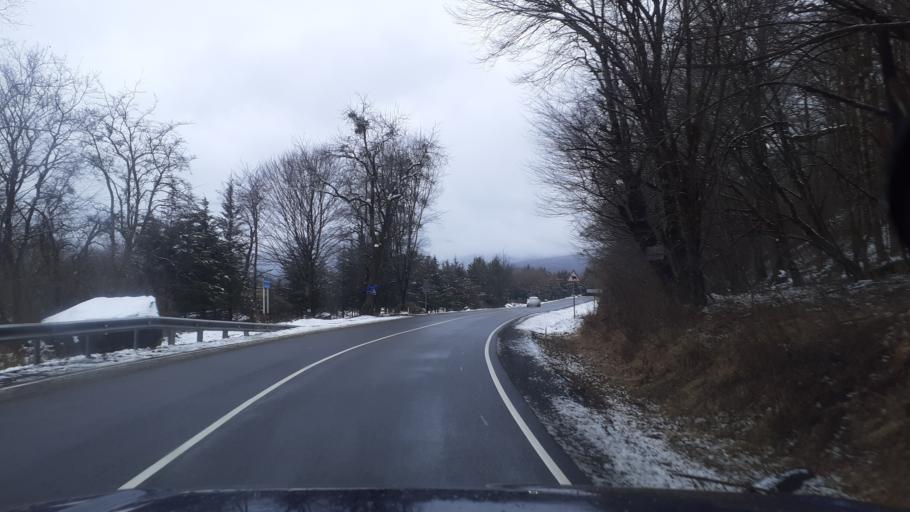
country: RU
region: Adygeya
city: Kamennomostskiy
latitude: 44.1171
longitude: 40.1211
